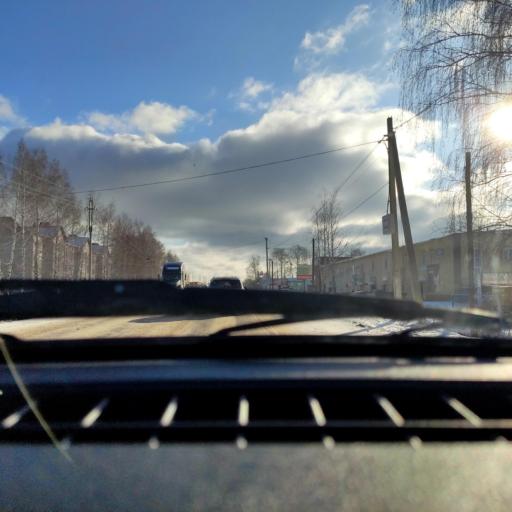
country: RU
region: Bashkortostan
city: Iglino
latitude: 54.8173
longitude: 56.4035
